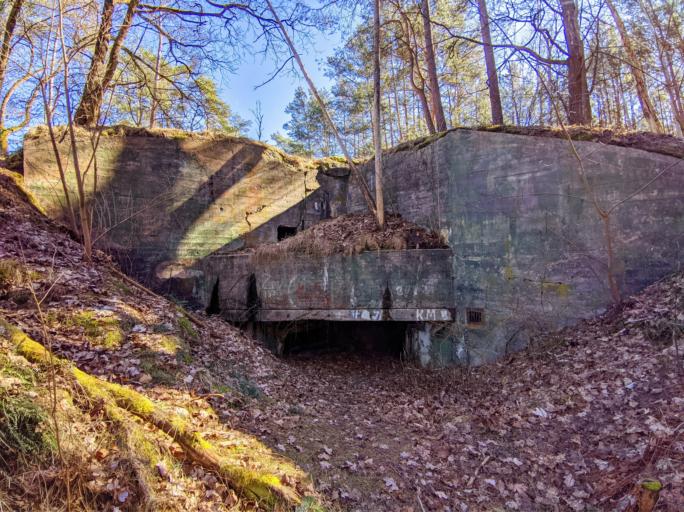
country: PL
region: Lubusz
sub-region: Powiat miedzyrzecki
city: Bledzew
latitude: 52.5887
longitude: 15.4254
